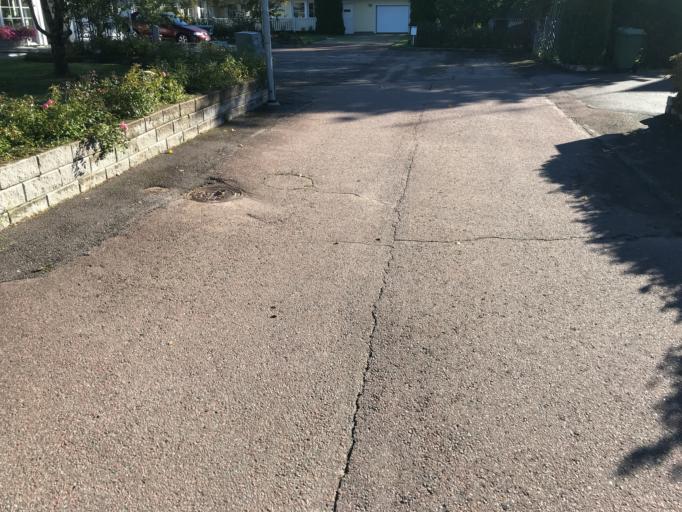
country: SE
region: Vaermland
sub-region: Karlstads Kommun
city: Karlstad
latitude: 59.3303
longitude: 13.5267
